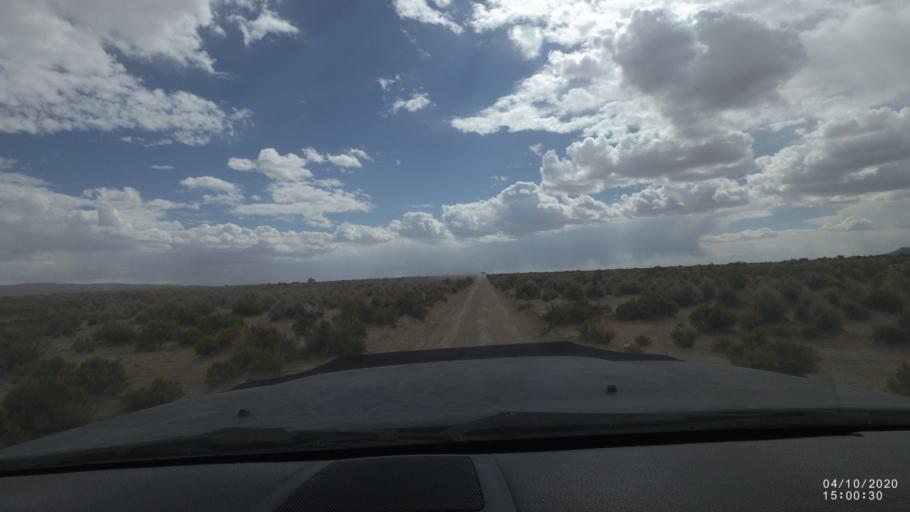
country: BO
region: Oruro
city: Poopo
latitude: -18.6865
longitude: -67.5276
